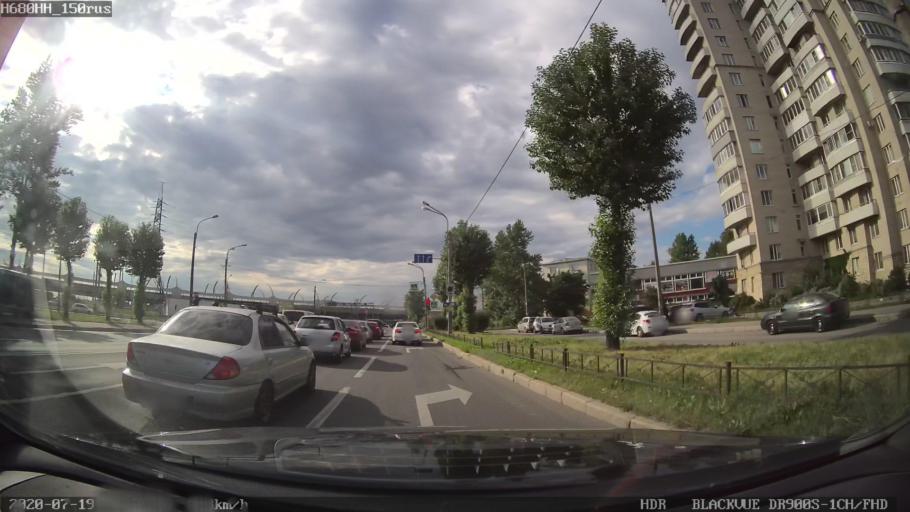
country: RU
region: St.-Petersburg
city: Avtovo
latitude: 59.8573
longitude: 30.2951
